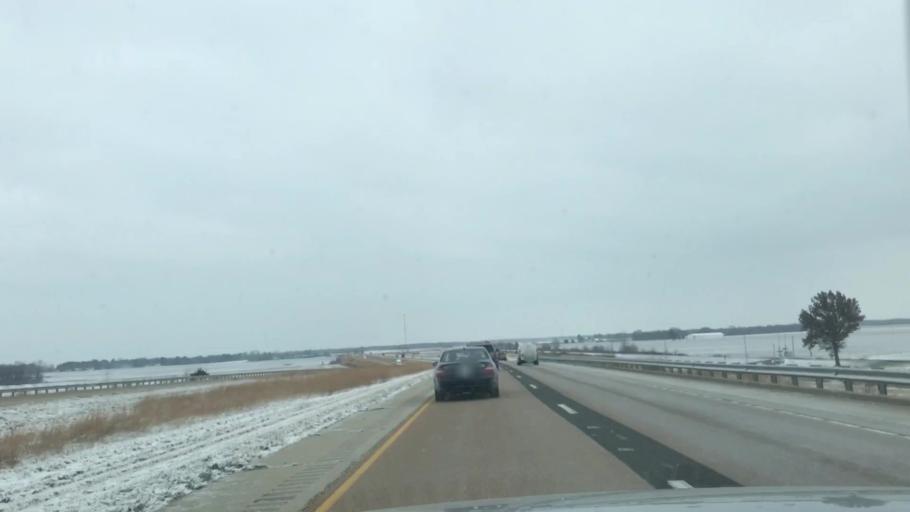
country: US
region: Illinois
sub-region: Montgomery County
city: Litchfield
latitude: 39.2176
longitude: -89.6498
